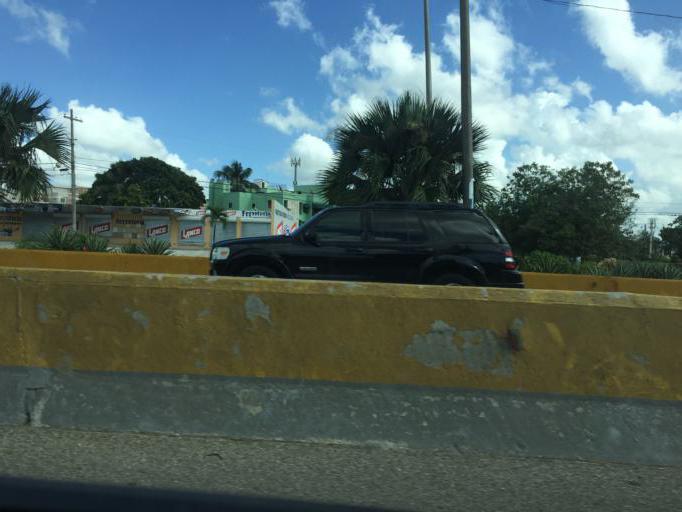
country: DO
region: Santo Domingo
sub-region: Santo Domingo
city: Santo Domingo Este
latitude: 18.4783
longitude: -69.8368
